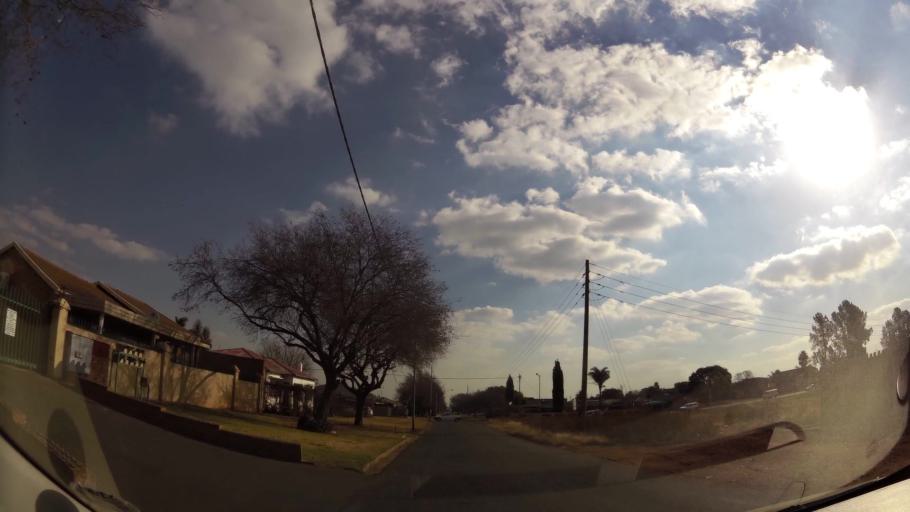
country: ZA
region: Gauteng
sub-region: West Rand District Municipality
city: Krugersdorp
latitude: -26.0849
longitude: 27.7683
